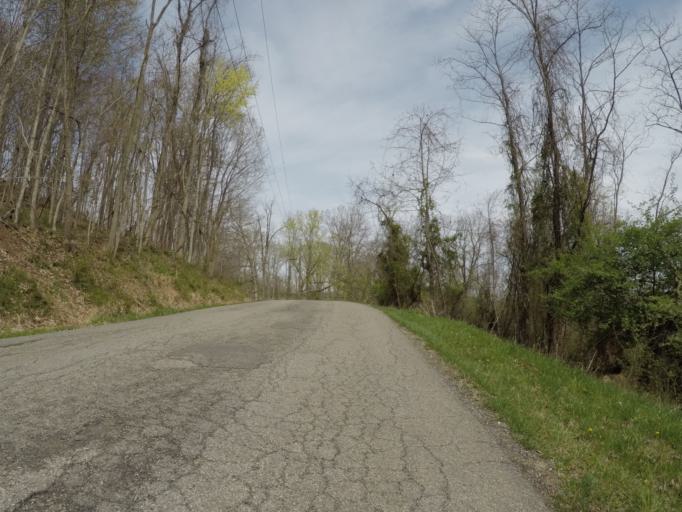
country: US
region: West Virginia
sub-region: Wayne County
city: Lavalette
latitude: 38.3535
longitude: -82.4004
